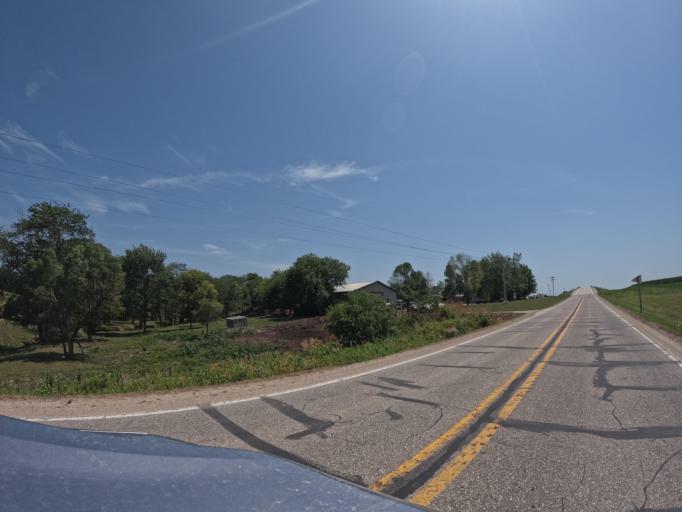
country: US
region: Iowa
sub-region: Henry County
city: Mount Pleasant
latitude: 40.9795
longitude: -91.6123
